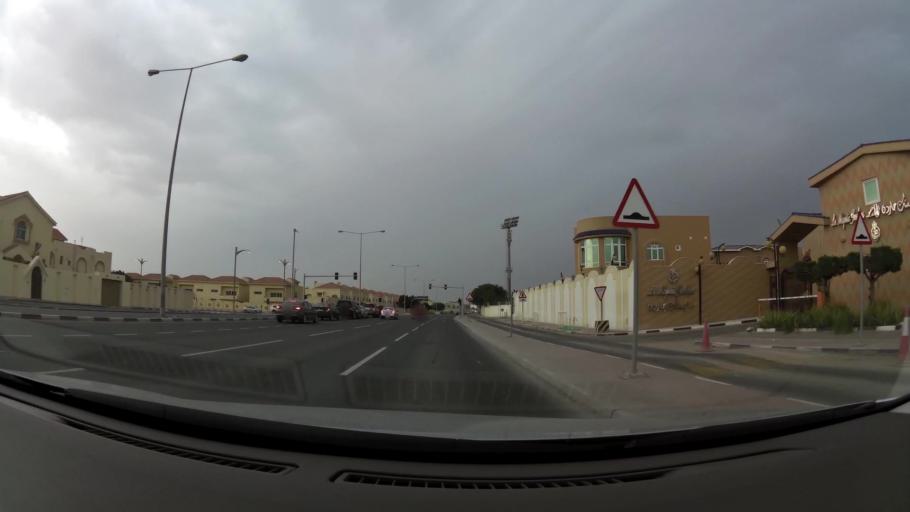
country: QA
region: Baladiyat ad Dawhah
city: Doha
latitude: 25.2609
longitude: 51.4814
